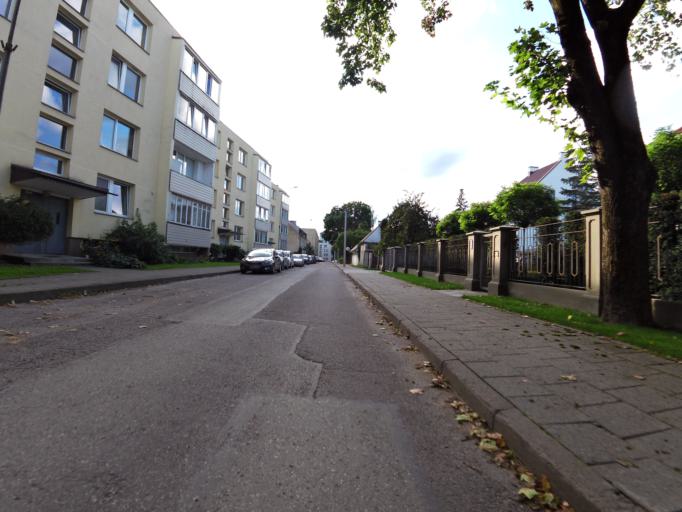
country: LT
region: Vilnius County
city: Naujamiestis
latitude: 54.6817
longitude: 25.2571
